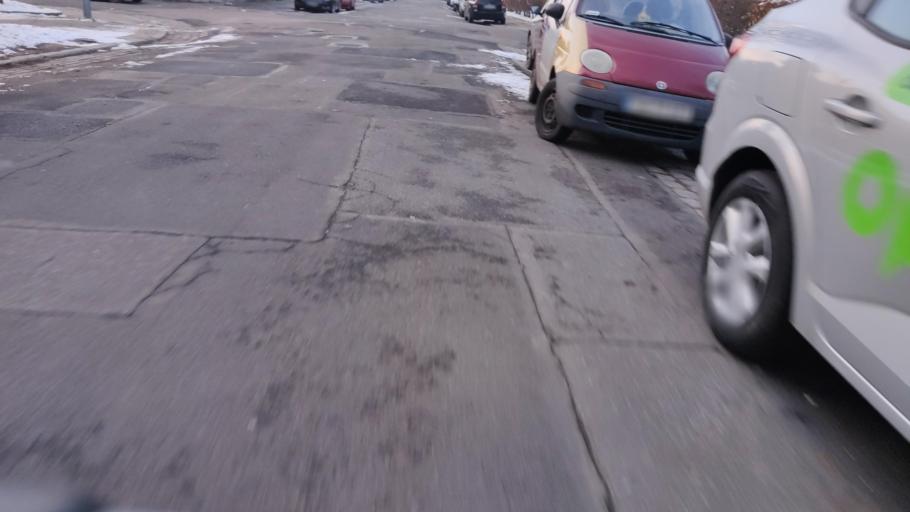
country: PL
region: Lower Silesian Voivodeship
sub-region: Powiat wroclawski
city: Wroclaw
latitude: 51.0827
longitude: 17.0075
